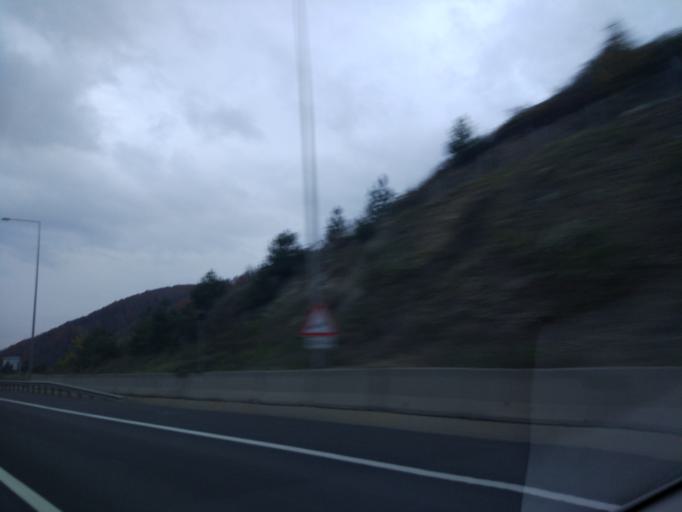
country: TR
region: Duzce
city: Kaynasli
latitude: 40.7663
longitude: 31.3774
